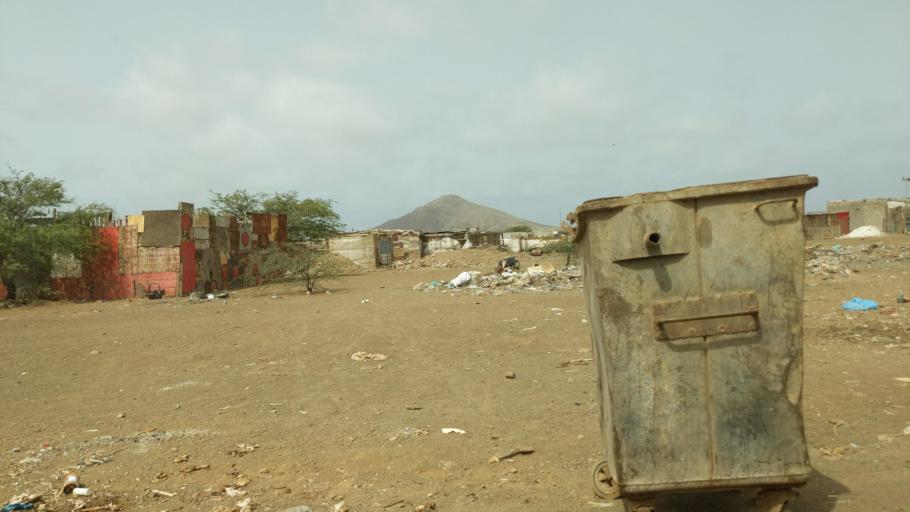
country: CV
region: Sal
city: Espargos
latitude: 16.7729
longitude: -22.9472
